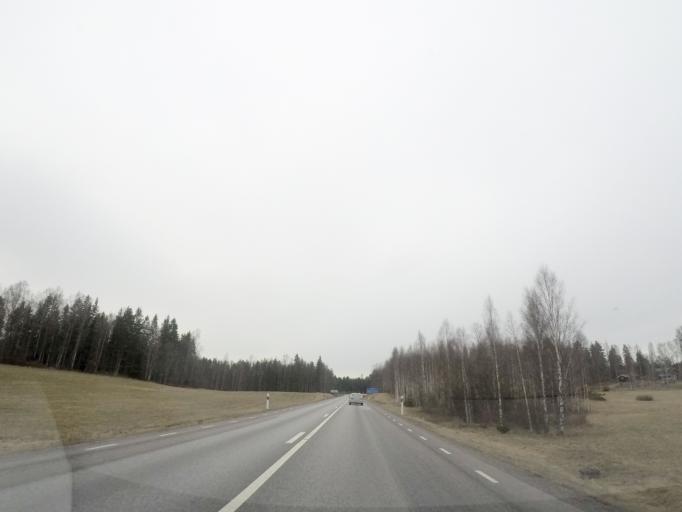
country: SE
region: Vaestmanland
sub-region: Skinnskattebergs Kommun
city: Skinnskatteberg
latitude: 59.8685
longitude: 15.6497
